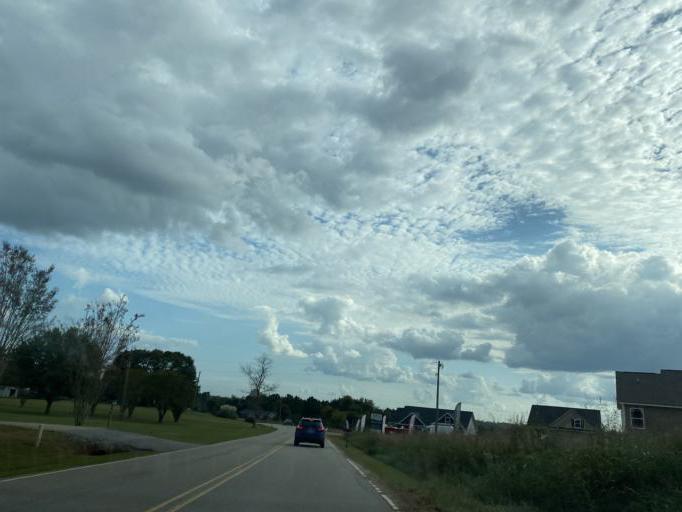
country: US
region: South Carolina
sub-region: Cherokee County
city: Gaffney
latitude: 35.0744
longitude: -81.7132
